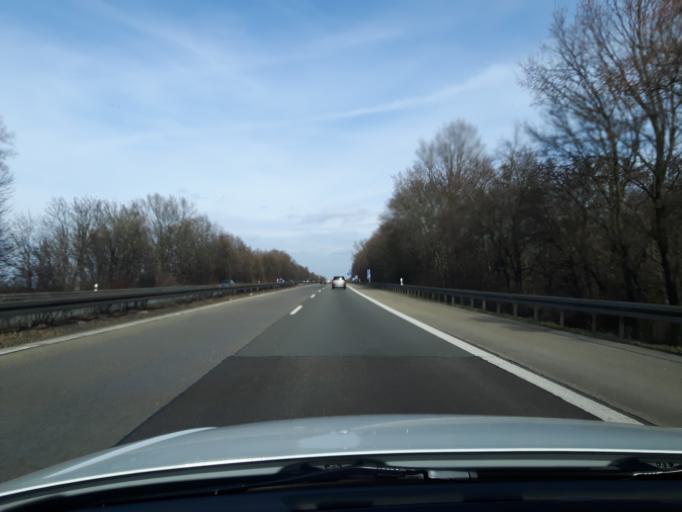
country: DE
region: North Rhine-Westphalia
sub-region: Regierungsbezirk Koln
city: Wahn-Heide
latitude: 50.8373
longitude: 7.0945
